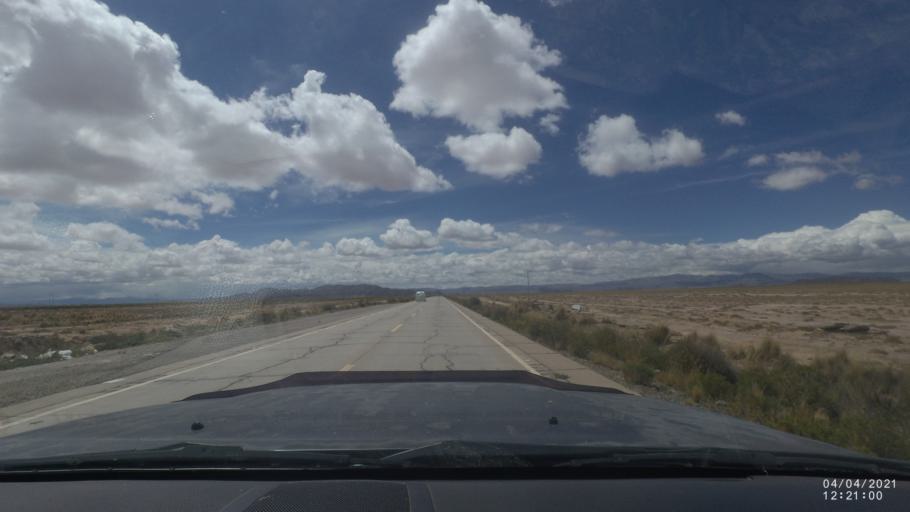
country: BO
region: Oruro
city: Oruro
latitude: -18.0719
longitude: -67.2243
